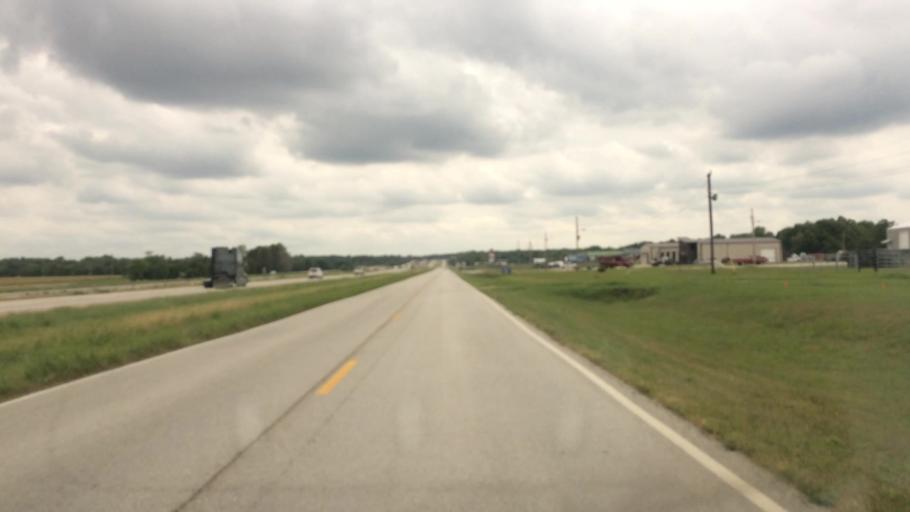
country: US
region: Missouri
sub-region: Greene County
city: Strafford
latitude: 37.2953
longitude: -93.0213
